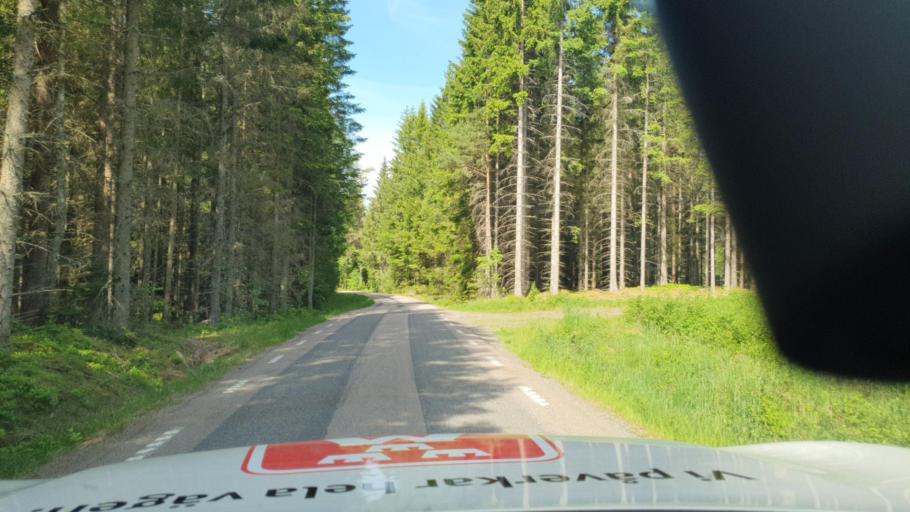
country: SE
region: Vaestra Goetaland
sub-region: Herrljunga Kommun
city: Herrljunga
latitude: 57.9255
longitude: 13.1030
